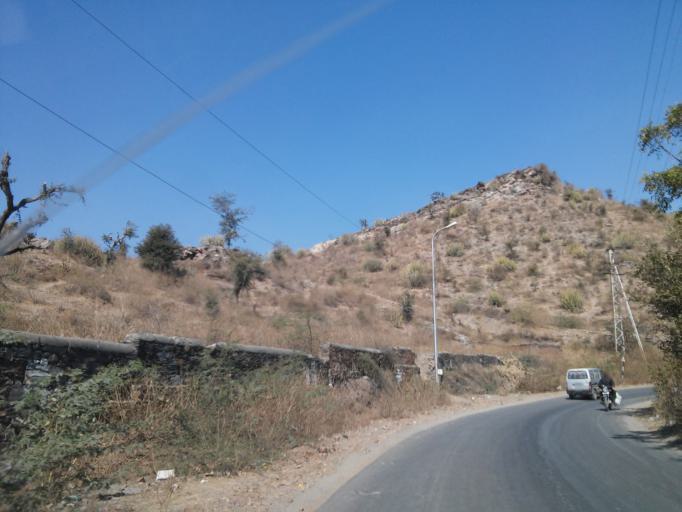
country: IN
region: Rajasthan
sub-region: Udaipur
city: Udaipur
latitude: 24.5735
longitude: 73.6541
